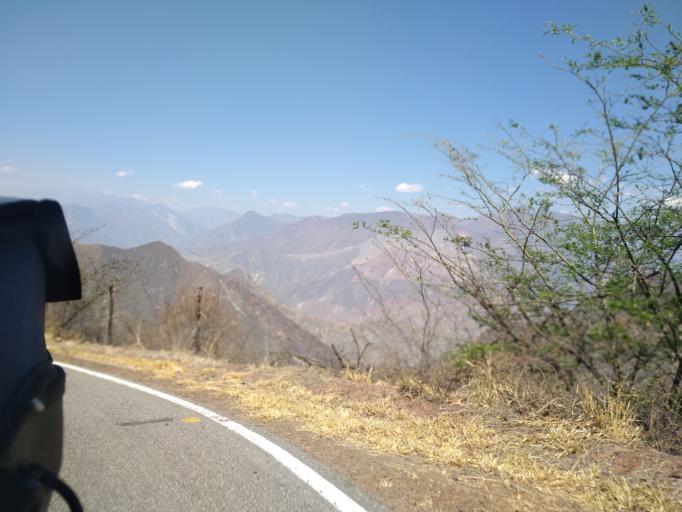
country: PE
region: Amazonas
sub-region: Provincia de Chachapoyas
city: Balsas
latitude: -6.8475
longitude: -77.9686
